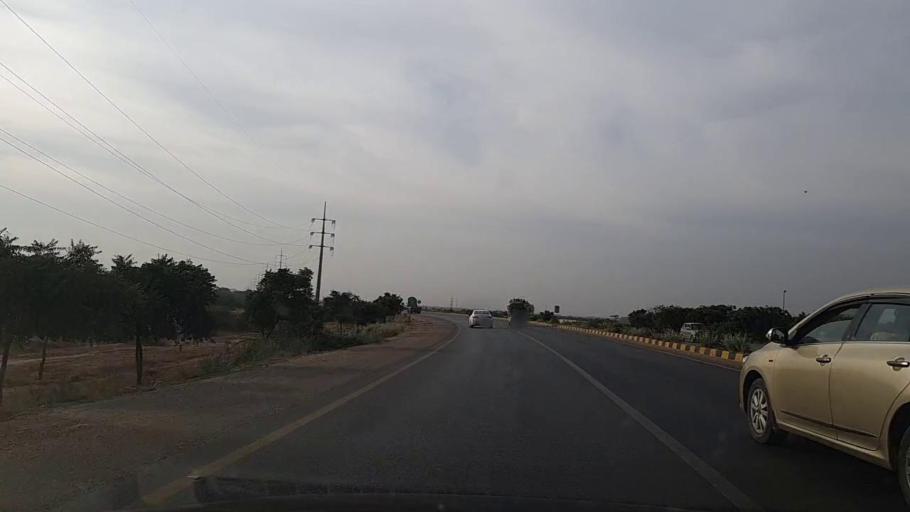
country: PK
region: Sindh
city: Gharo
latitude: 24.8365
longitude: 67.4531
